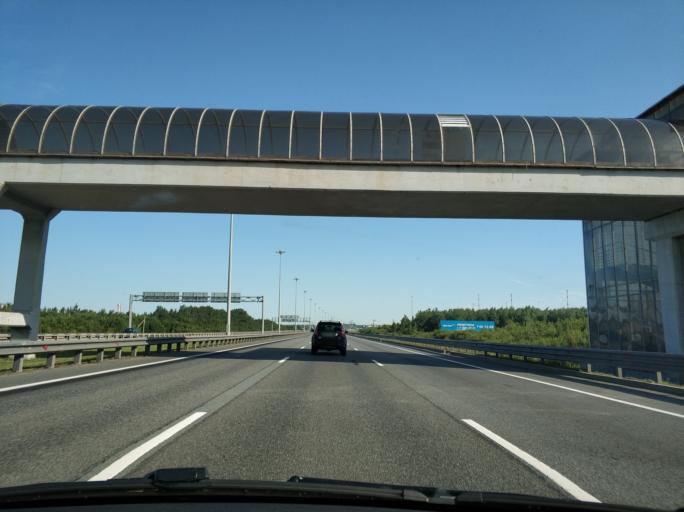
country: RU
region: Leningrad
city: Bugry
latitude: 60.0679
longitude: 30.3843
